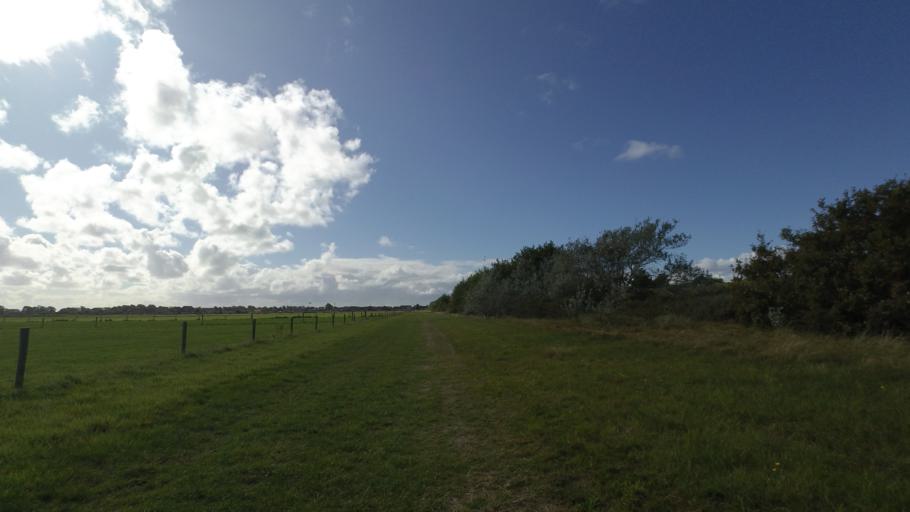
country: NL
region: Friesland
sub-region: Gemeente Ameland
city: Nes
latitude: 53.4514
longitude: 5.8127
